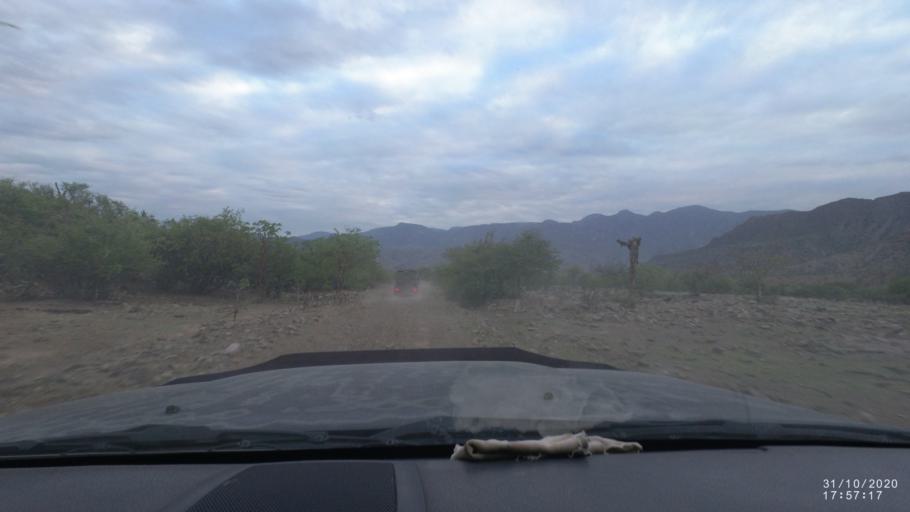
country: BO
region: Chuquisaca
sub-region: Provincia Zudanez
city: Mojocoya
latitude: -18.6499
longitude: -64.5319
